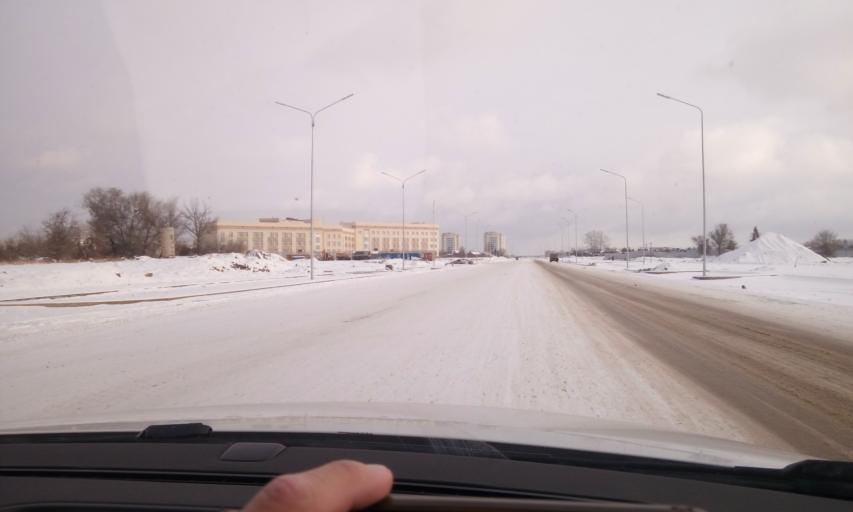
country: KZ
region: Astana Qalasy
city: Astana
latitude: 51.1214
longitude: 71.4904
